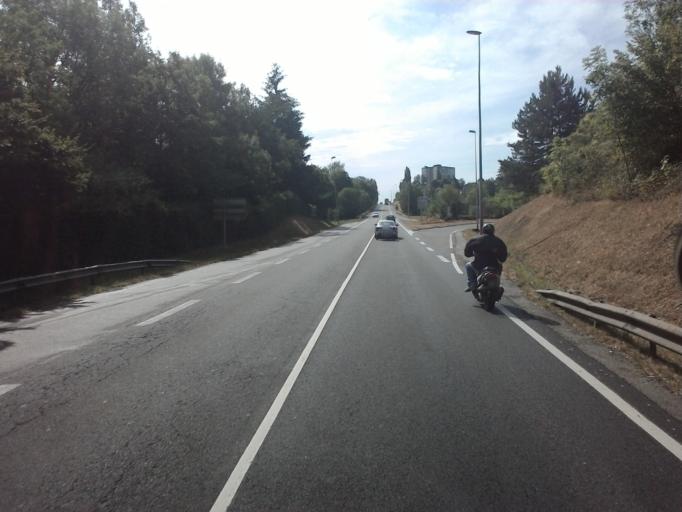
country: FR
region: Franche-Comte
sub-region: Departement du Jura
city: Lons-le-Saunier
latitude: 46.6856
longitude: 5.5660
